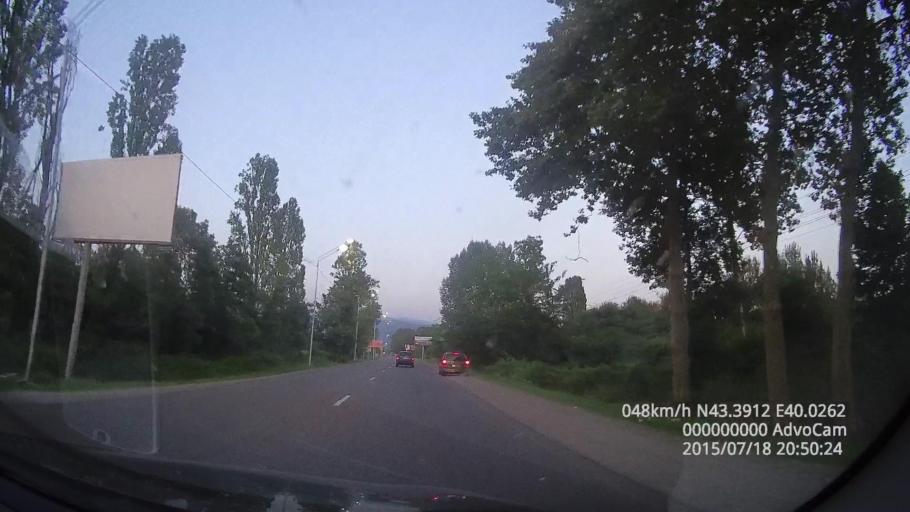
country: GE
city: Gantiadi
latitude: 43.3910
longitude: 40.0276
